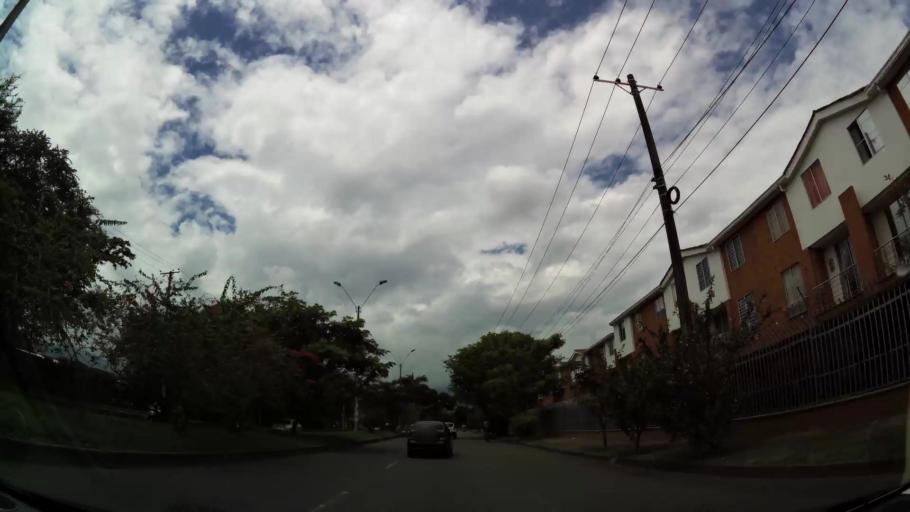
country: CO
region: Valle del Cauca
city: Cali
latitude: 3.3931
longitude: -76.5297
